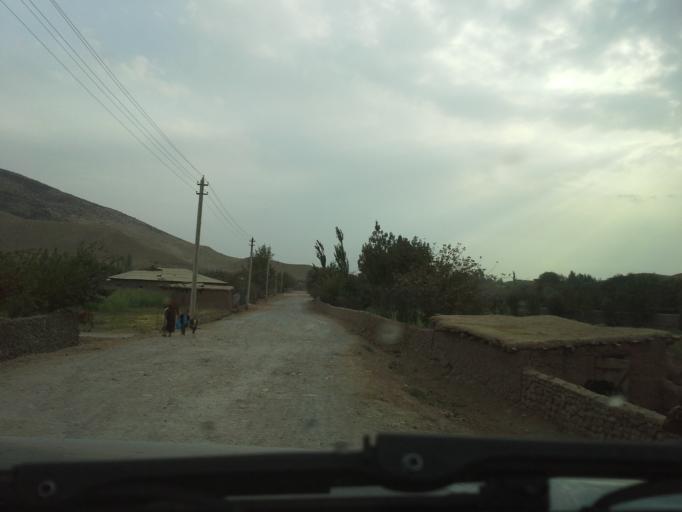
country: UZ
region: Qashqadaryo
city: Qorashina
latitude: 37.9305
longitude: 66.4970
